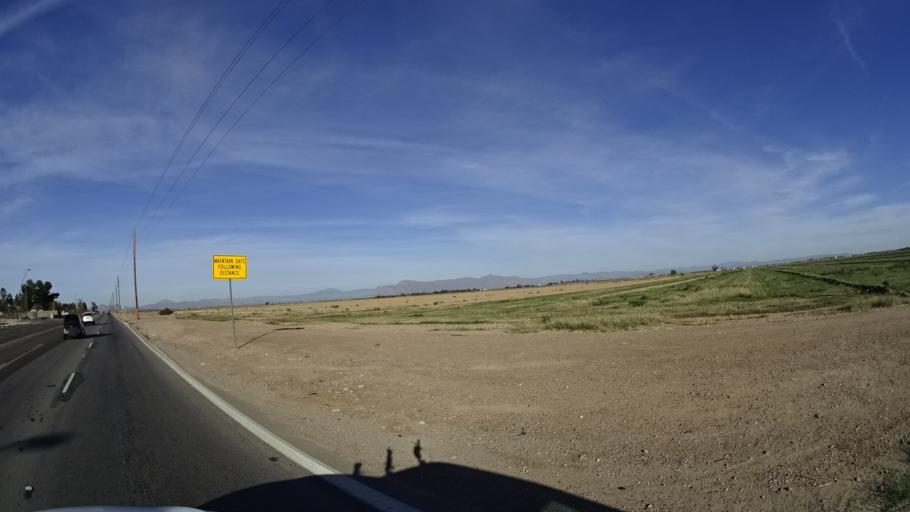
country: US
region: Arizona
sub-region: Maricopa County
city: Queen Creek
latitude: 33.2695
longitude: -111.6348
